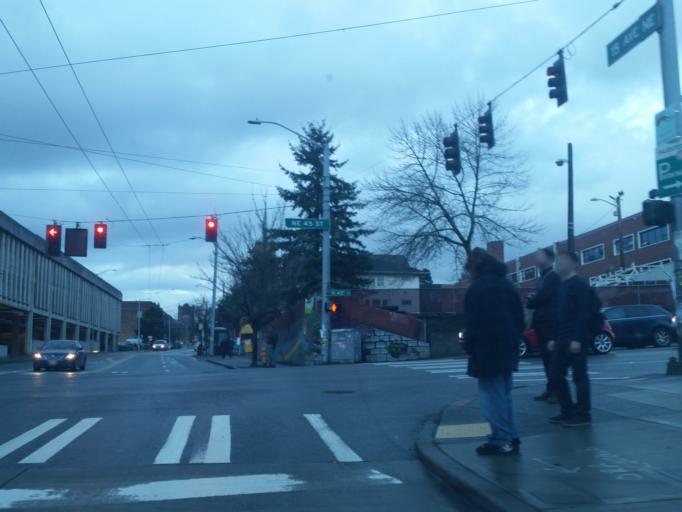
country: US
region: Washington
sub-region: King County
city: Seattle
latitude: 47.6612
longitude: -122.3119
